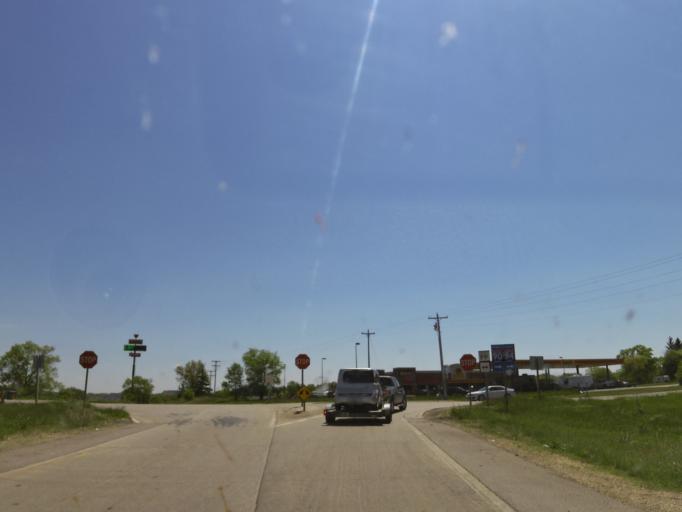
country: US
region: Wisconsin
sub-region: Monroe County
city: Tomah
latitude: 43.9621
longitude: -90.3788
